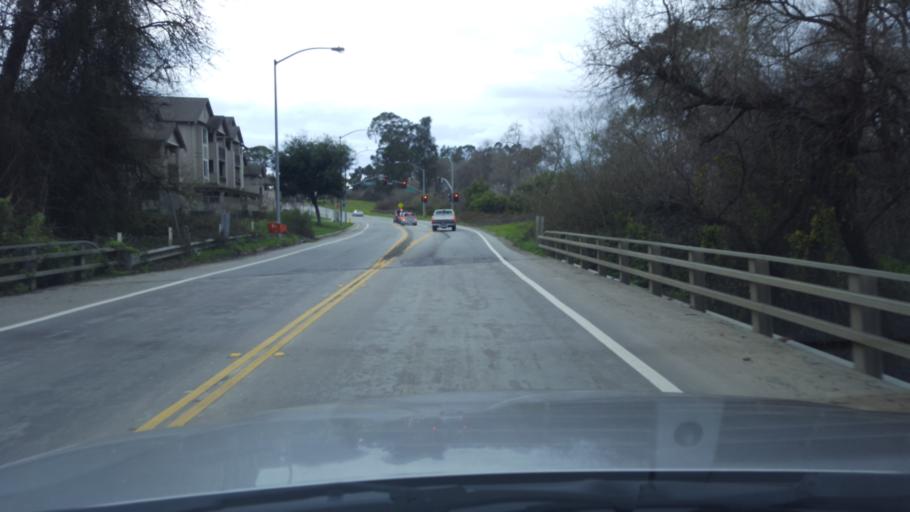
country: US
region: California
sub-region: Santa Cruz County
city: Freedom
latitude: 36.9415
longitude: -121.7733
